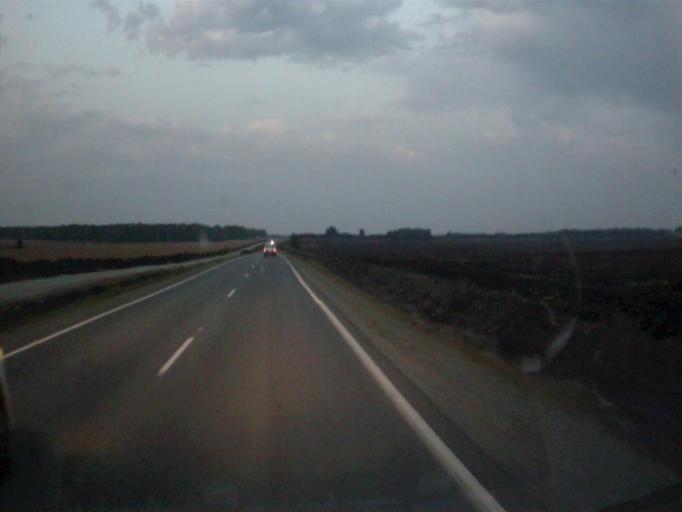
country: RU
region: Chelyabinsk
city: Timiryazevskiy
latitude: 55.2077
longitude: 60.8131
